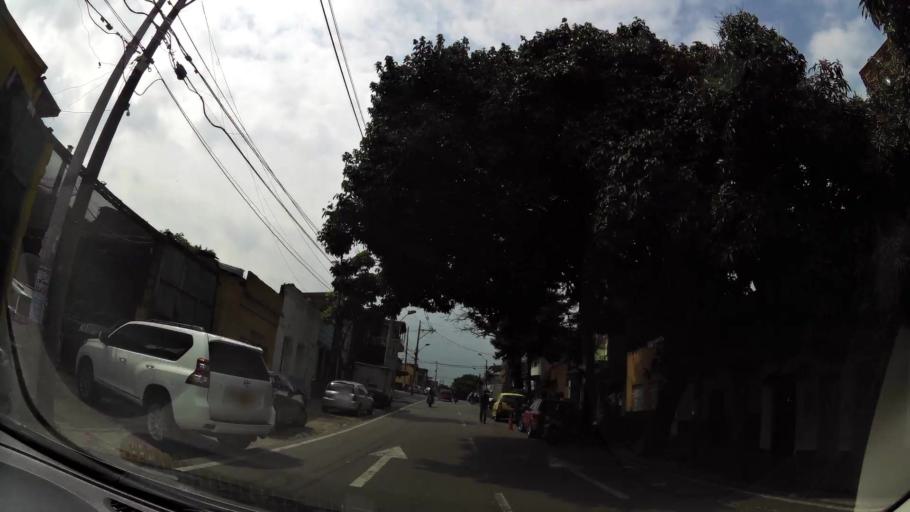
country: CO
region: Antioquia
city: Medellin
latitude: 6.2659
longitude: -75.5601
